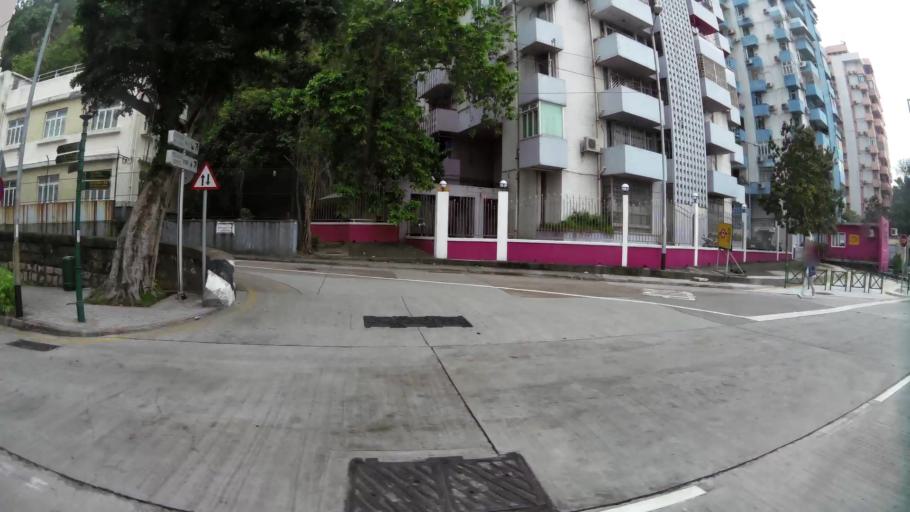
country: CN
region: Guangdong
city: Wanzai
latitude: 22.1841
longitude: 113.5311
